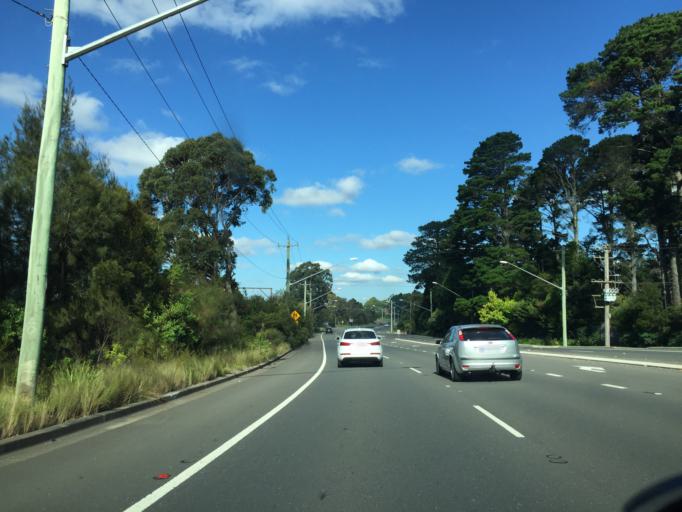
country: AU
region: New South Wales
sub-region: Blue Mountains Municipality
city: Leura
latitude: -33.7109
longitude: 150.3566
